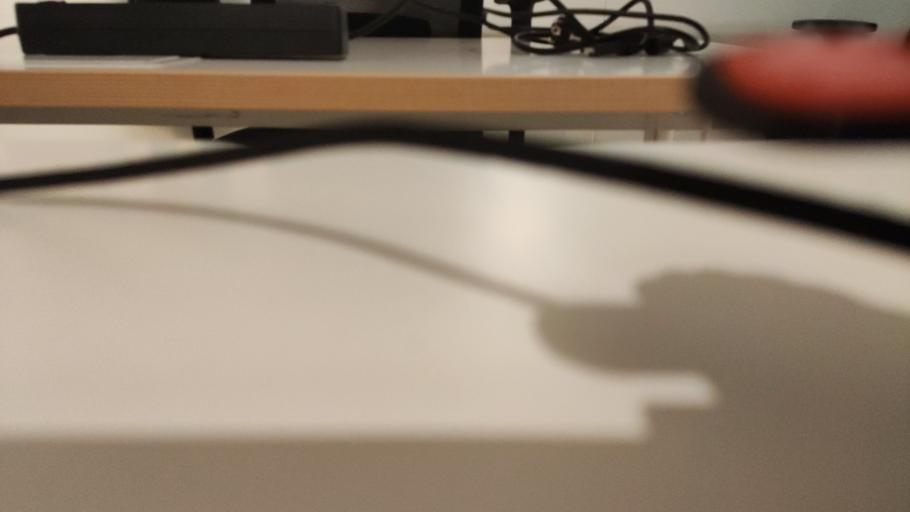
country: RU
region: Moskovskaya
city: Proletarskiy
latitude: 54.9778
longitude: 37.3509
